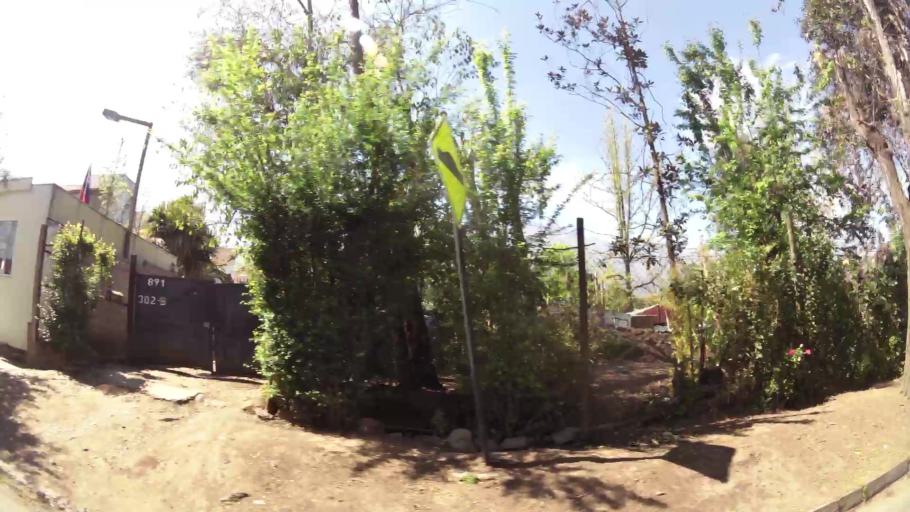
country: CL
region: Santiago Metropolitan
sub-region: Provincia de Santiago
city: Villa Presidente Frei, Nunoa, Santiago, Chile
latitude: -33.4460
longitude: -70.5273
